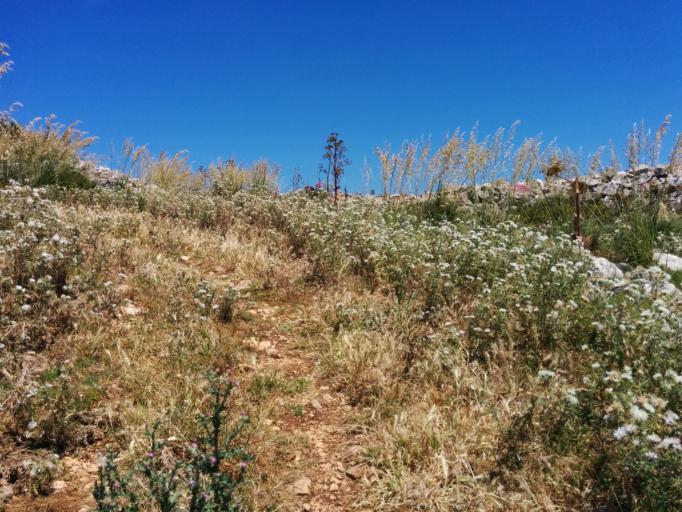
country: IT
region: Sicily
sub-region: Trapani
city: San Vito Lo Capo
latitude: 38.1664
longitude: 12.7580
